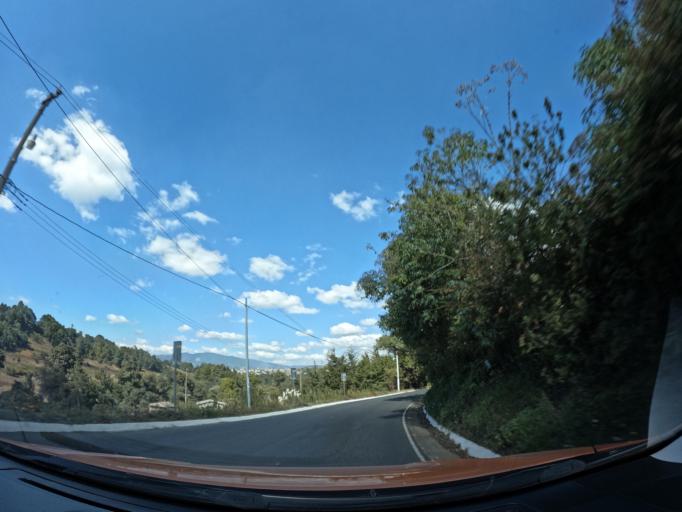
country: GT
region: Chimaltenango
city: Patzun
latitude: 14.6595
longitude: -91.0194
